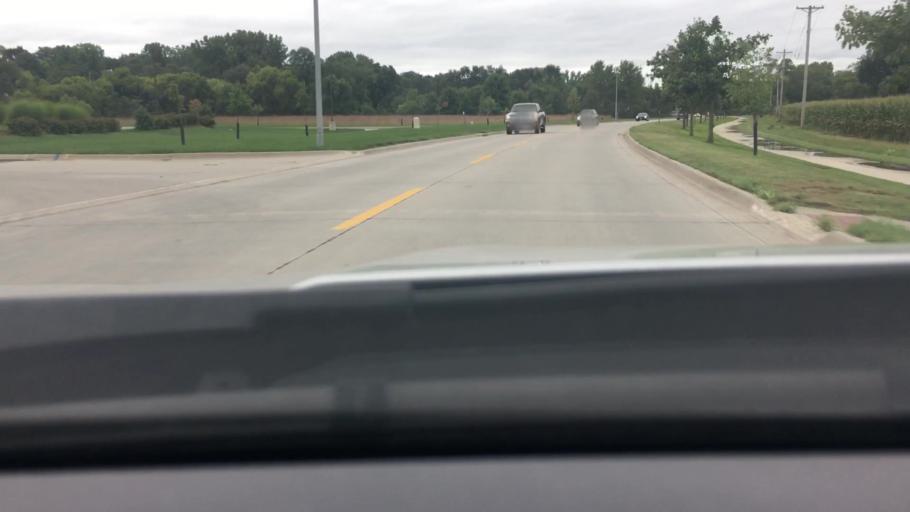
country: US
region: Iowa
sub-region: Pottawattamie County
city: Council Bluffs
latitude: 41.2643
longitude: -95.8041
